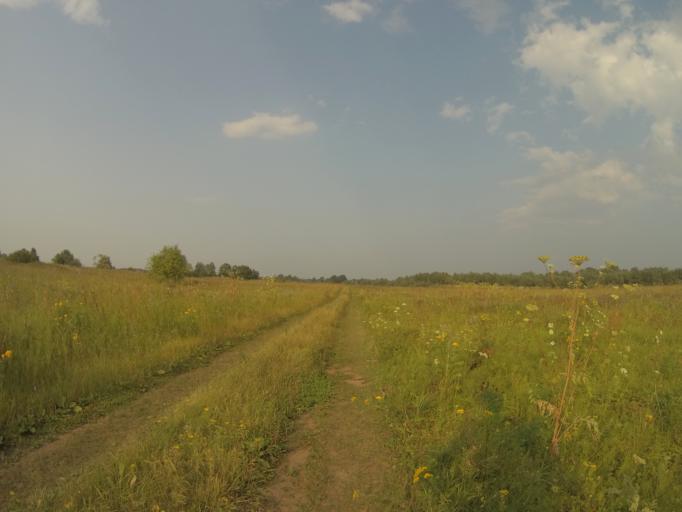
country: RU
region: Vladimir
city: Kommunar
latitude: 56.0954
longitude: 40.4130
